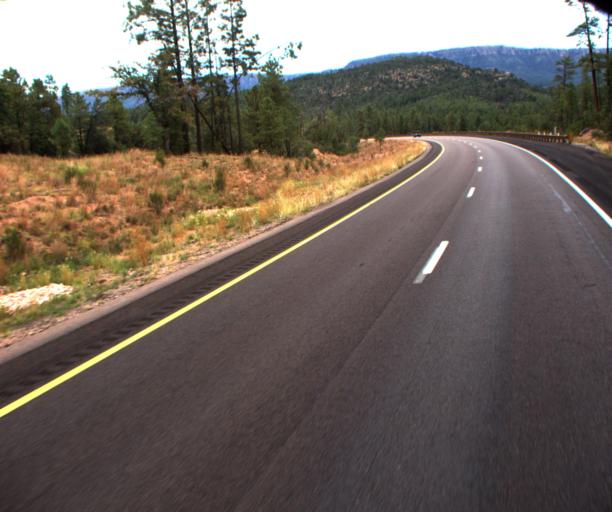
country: US
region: Arizona
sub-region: Gila County
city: Star Valley
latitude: 34.3025
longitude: -111.1110
